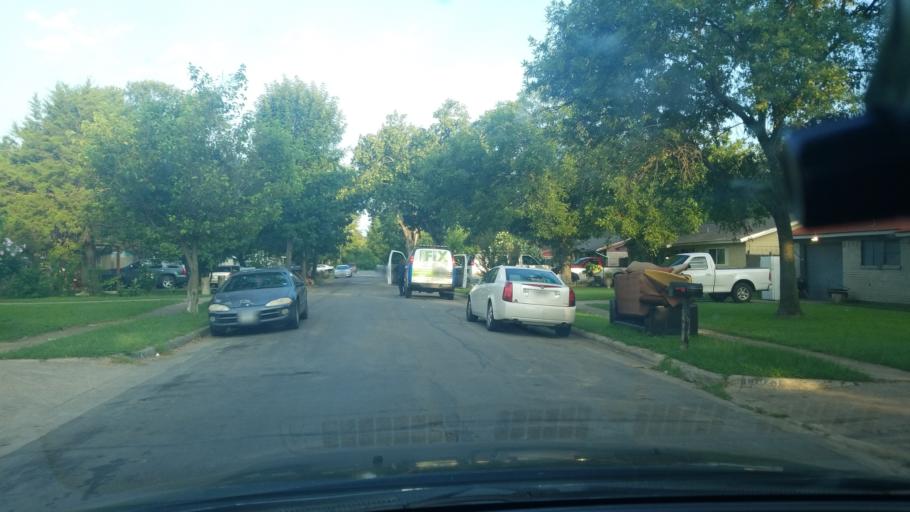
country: US
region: Texas
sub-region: Dallas County
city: Balch Springs
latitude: 32.7246
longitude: -96.6505
